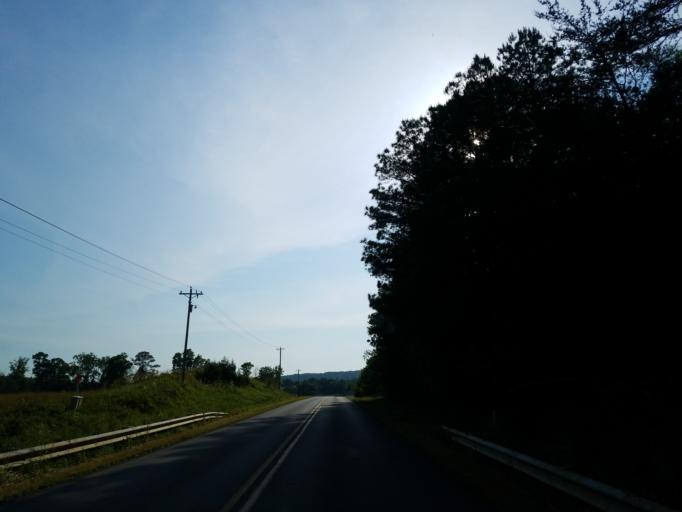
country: US
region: Georgia
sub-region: Chattooga County
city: Trion
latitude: 34.5640
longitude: -85.1752
